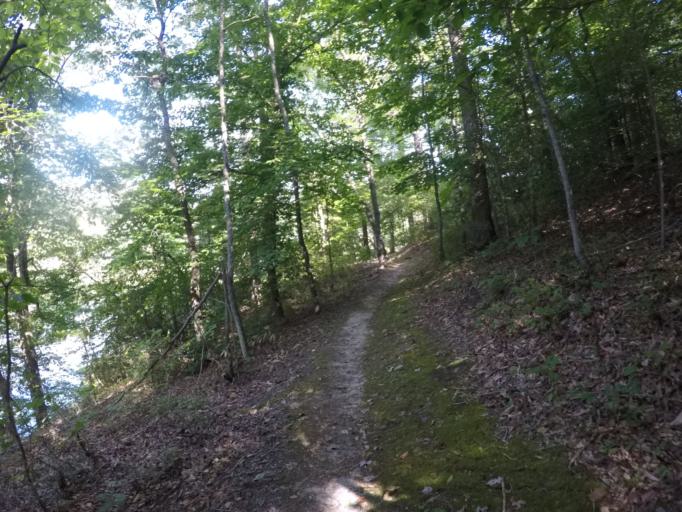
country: US
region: Ohio
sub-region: Lawrence County
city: Ironton
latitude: 38.6171
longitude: -82.6225
